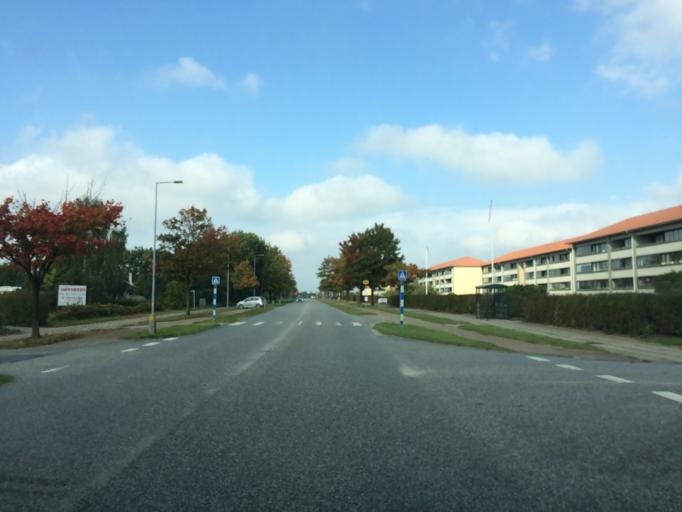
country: DK
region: Central Jutland
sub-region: Skive Kommune
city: Skive
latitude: 56.5469
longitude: 9.0206
